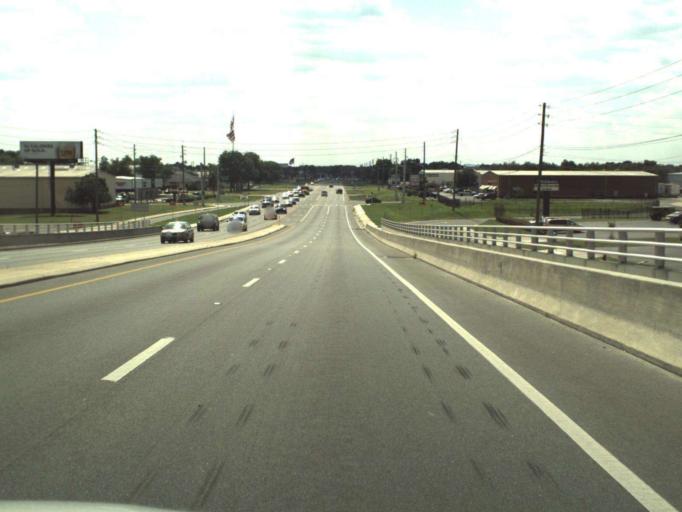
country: US
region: Florida
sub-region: Marion County
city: Ocala
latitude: 29.1717
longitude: -82.1460
